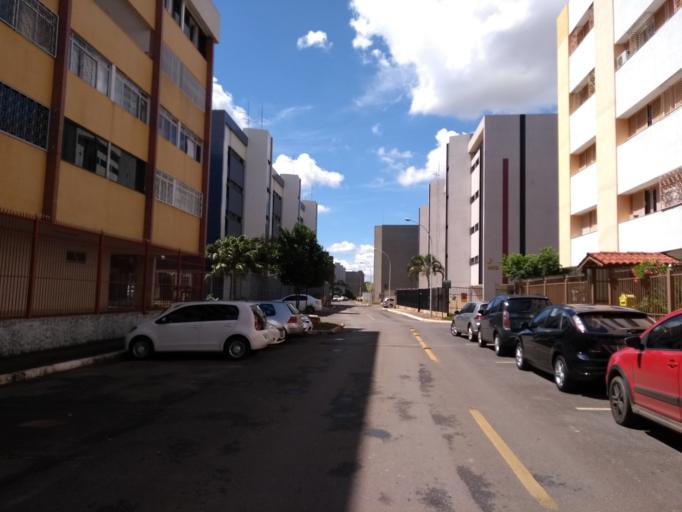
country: BR
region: Federal District
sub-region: Brasilia
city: Brasilia
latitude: -15.7947
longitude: -47.9345
